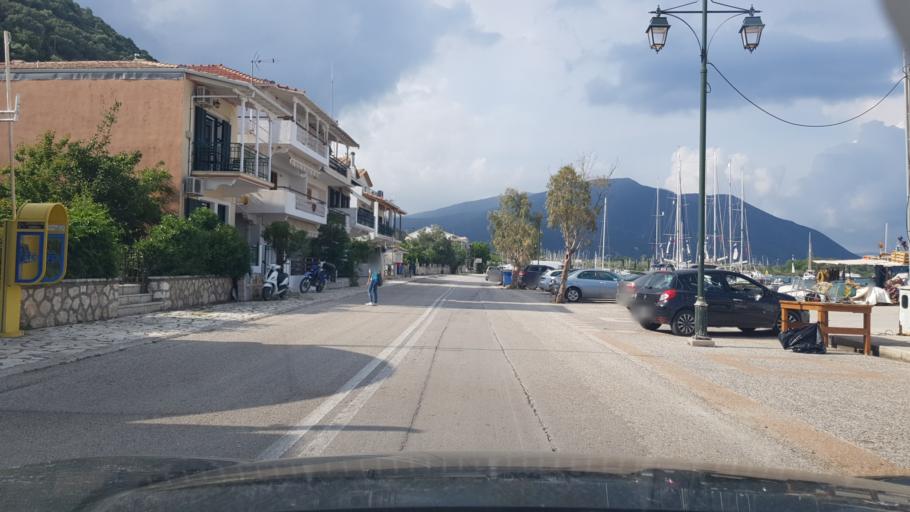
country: GR
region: Ionian Islands
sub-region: Lefkada
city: Nidri
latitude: 38.6855
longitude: 20.6985
